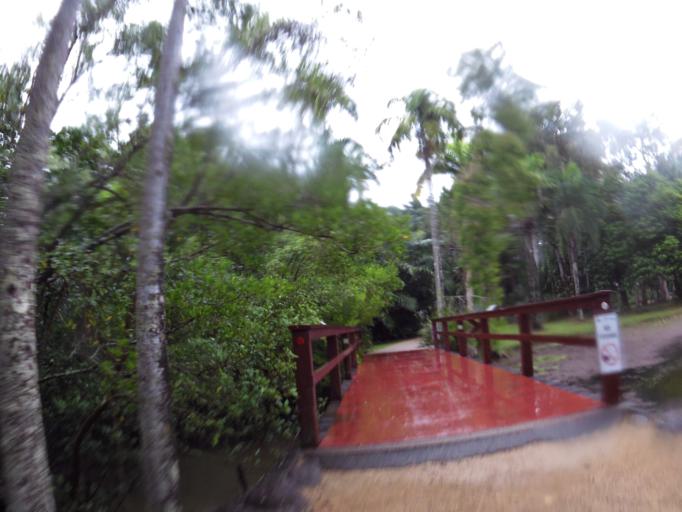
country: AU
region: Queensland
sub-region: Cairns
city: Cairns
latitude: -16.9027
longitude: 145.7504
